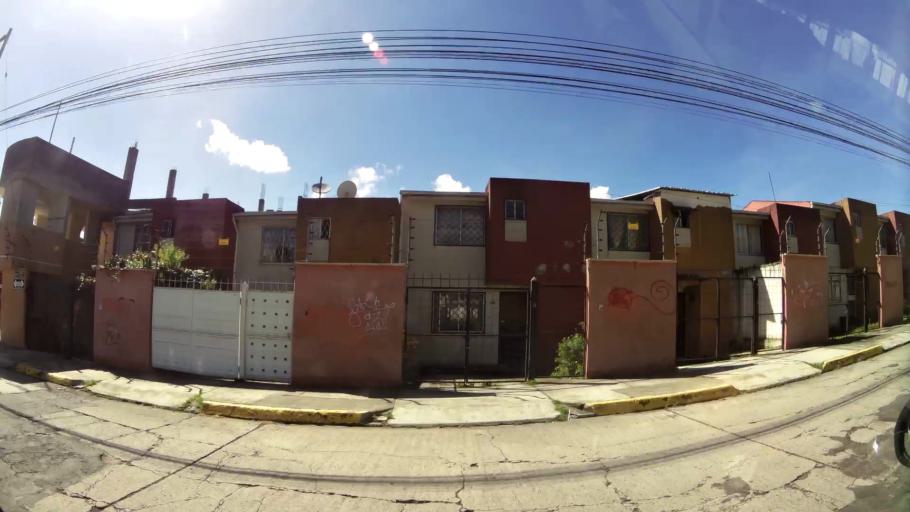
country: EC
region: Pichincha
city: Quito
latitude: -0.2894
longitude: -78.5586
